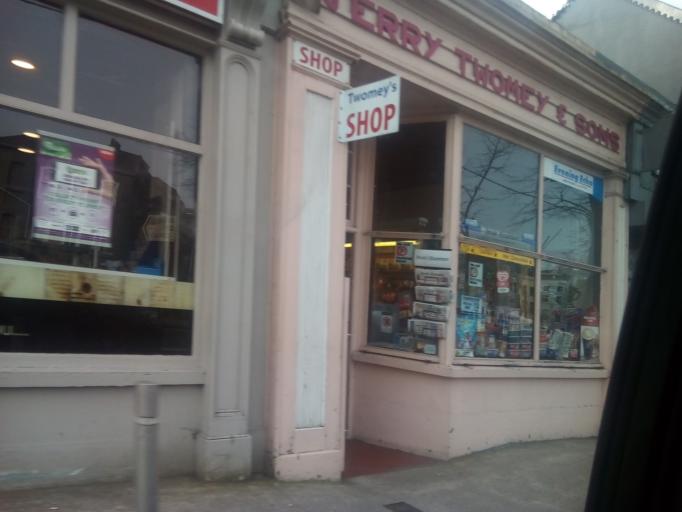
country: IE
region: Munster
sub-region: County Cork
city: Cork
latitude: 51.8954
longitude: -8.4726
